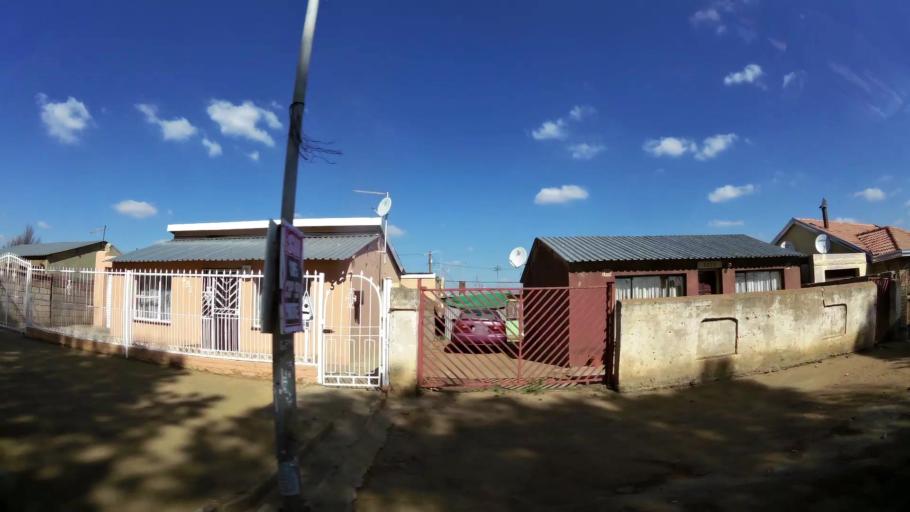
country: ZA
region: Gauteng
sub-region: West Rand District Municipality
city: Krugersdorp
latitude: -26.1543
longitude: 27.7740
